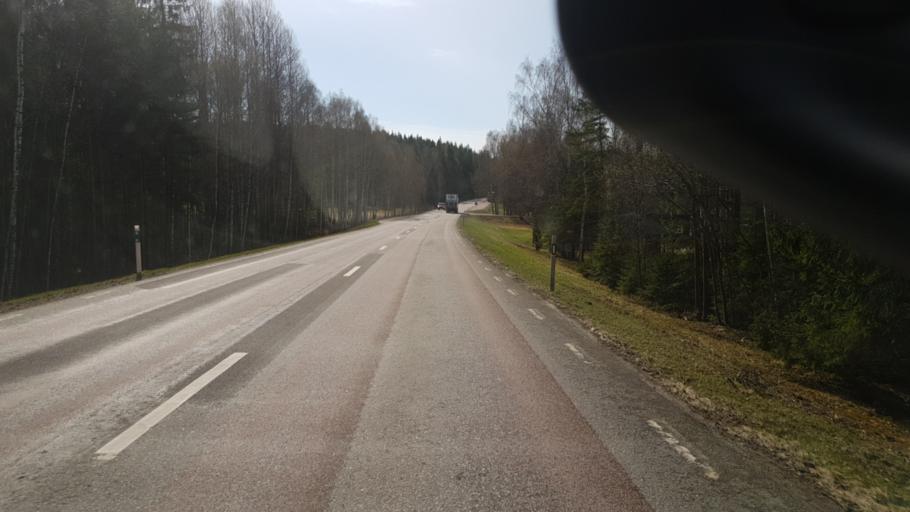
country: SE
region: Vaermland
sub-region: Arvika Kommun
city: Arvika
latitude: 59.5814
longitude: 12.7042
